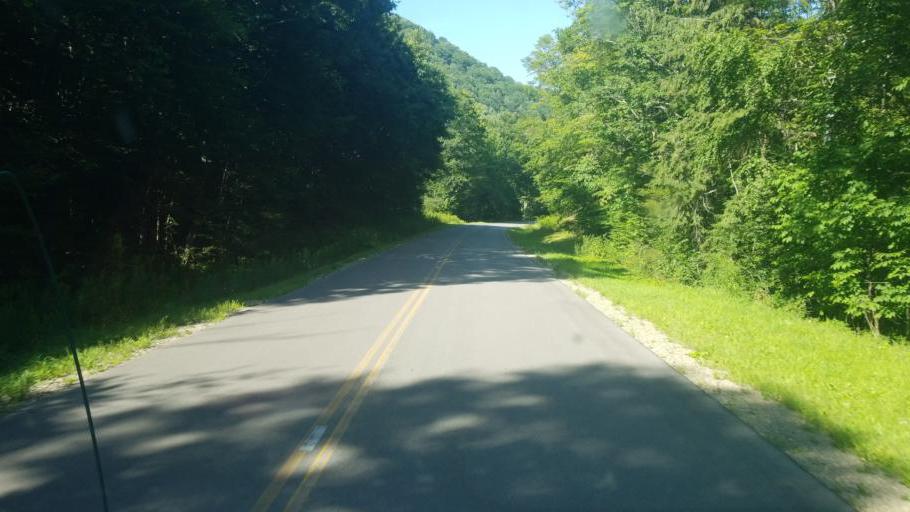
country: US
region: New York
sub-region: Allegany County
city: Wellsville
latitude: 42.0184
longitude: -77.9867
